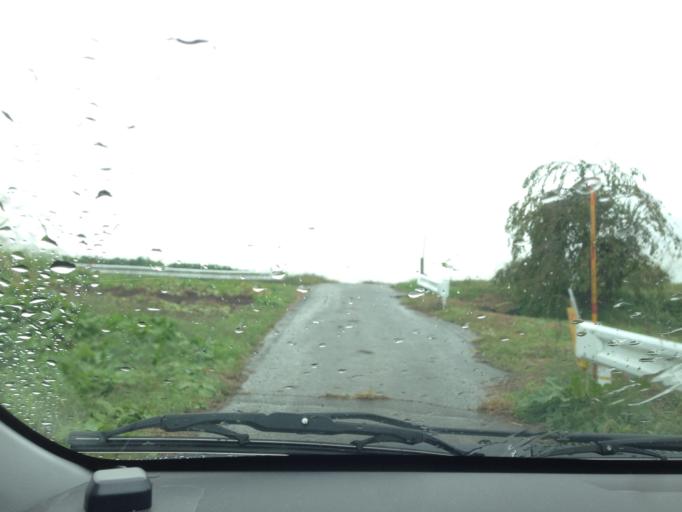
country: JP
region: Fukushima
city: Kitakata
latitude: 37.5254
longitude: 139.8318
